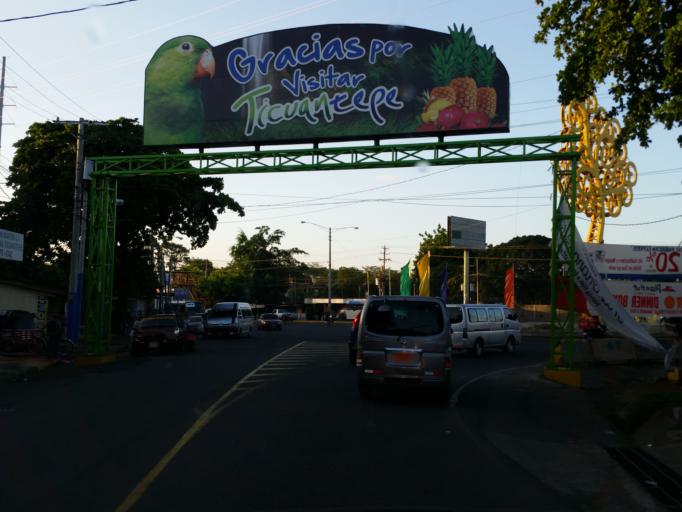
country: NI
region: Masaya
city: Ticuantepe
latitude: 12.0552
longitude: -86.2032
